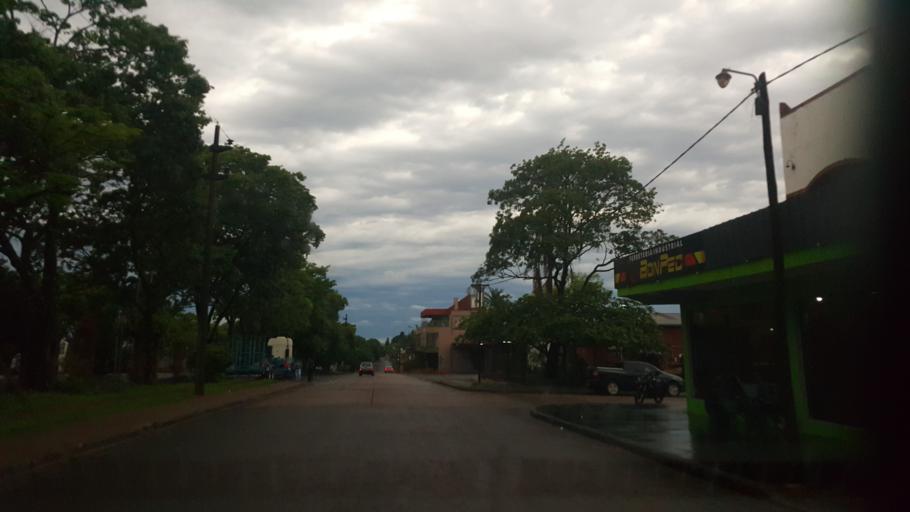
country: AR
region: Misiones
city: Jardin America
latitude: -27.0462
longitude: -55.2402
